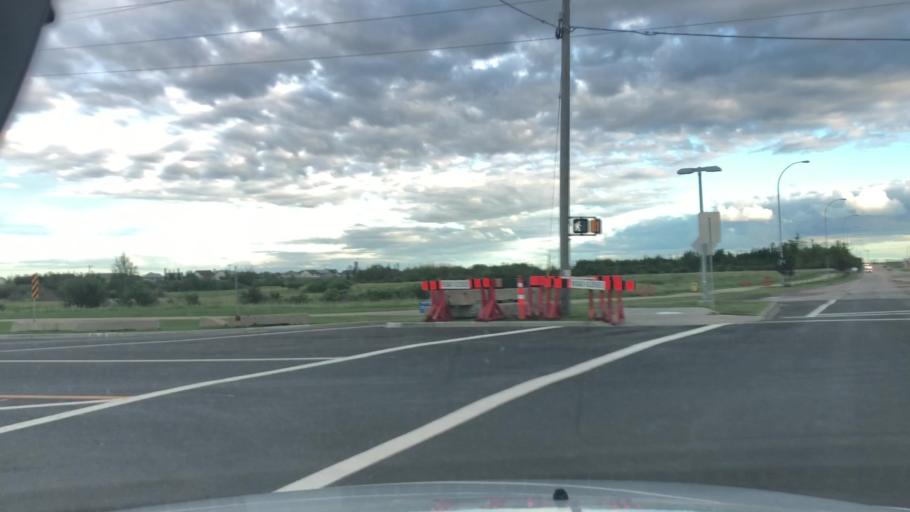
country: CA
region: Alberta
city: St. Albert
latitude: 53.6146
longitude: -113.5697
